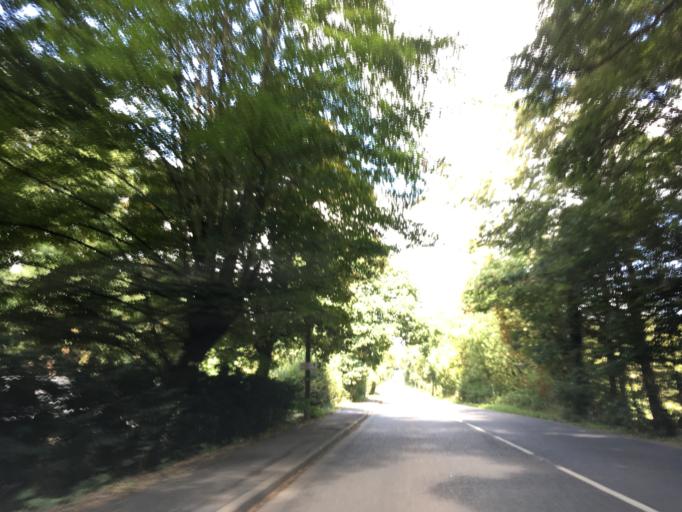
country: GB
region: England
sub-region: Hampshire
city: Colden Common
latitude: 50.9876
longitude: -1.3064
